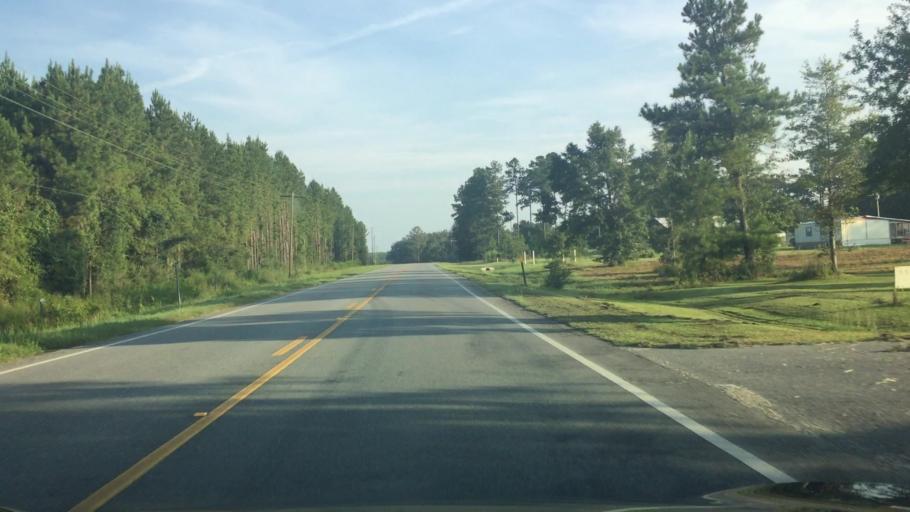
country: US
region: Alabama
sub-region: Covington County
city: Florala
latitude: 31.0199
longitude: -86.3632
